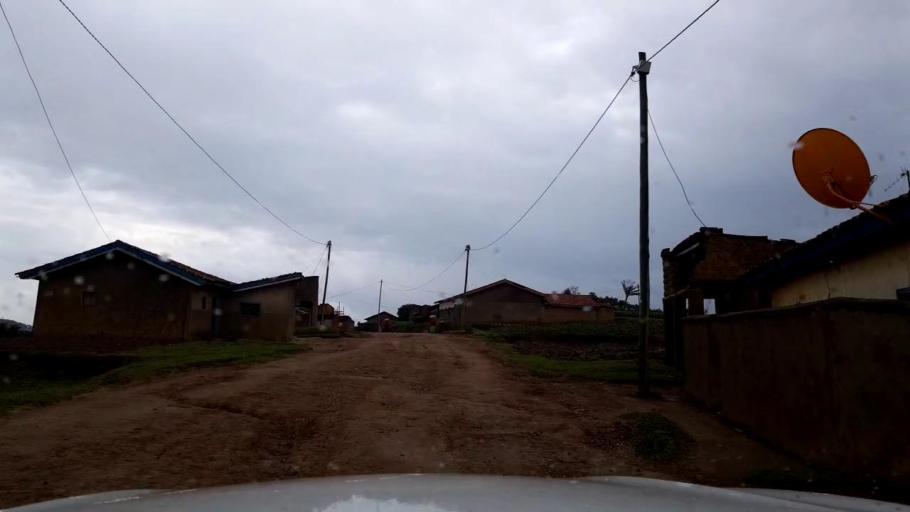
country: RW
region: Western Province
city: Kibuye
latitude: -2.0126
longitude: 29.4720
